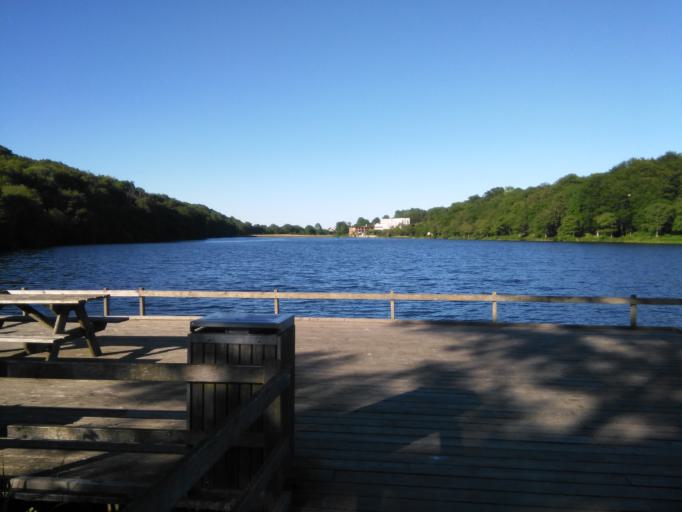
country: DK
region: Capital Region
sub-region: Bornholm Kommune
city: Ronne
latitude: 55.2816
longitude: 14.7617
